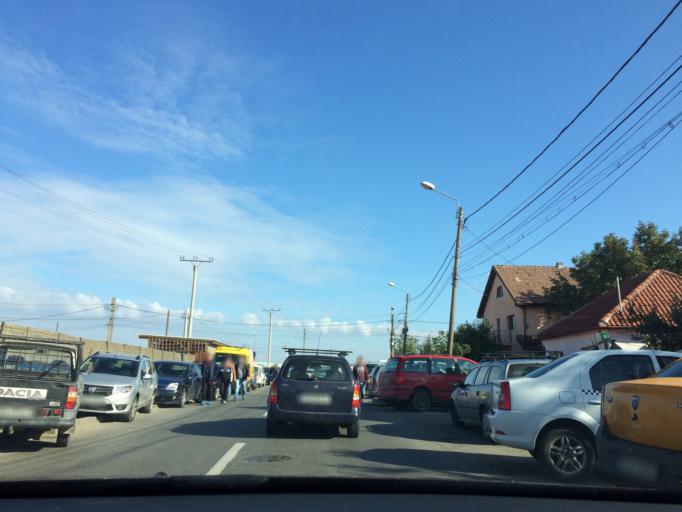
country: RO
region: Timis
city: Timisoara
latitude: 45.7694
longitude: 21.1961
